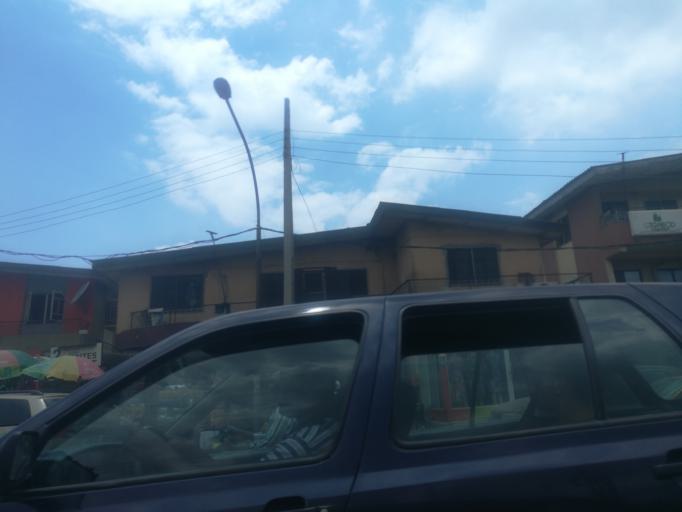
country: NG
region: Lagos
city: Somolu
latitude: 6.5520
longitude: 3.3921
